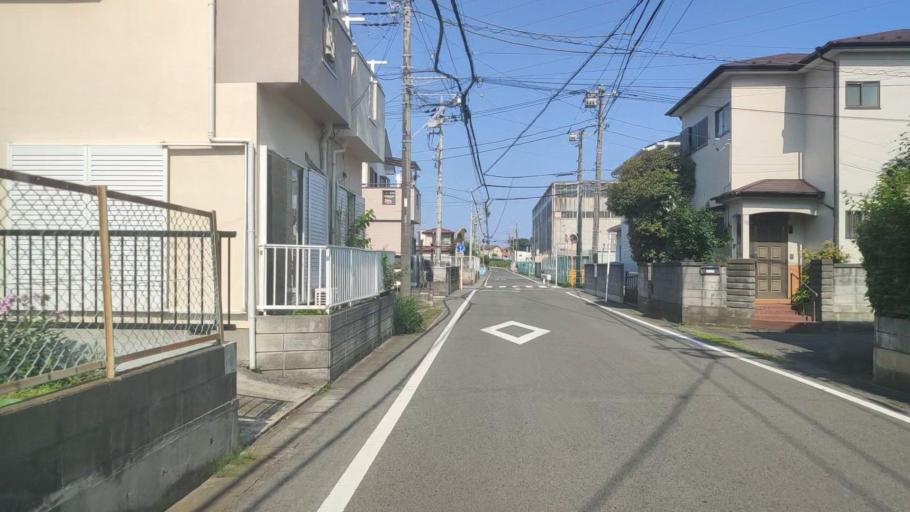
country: JP
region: Kanagawa
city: Hiratsuka
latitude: 35.3513
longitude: 139.3261
